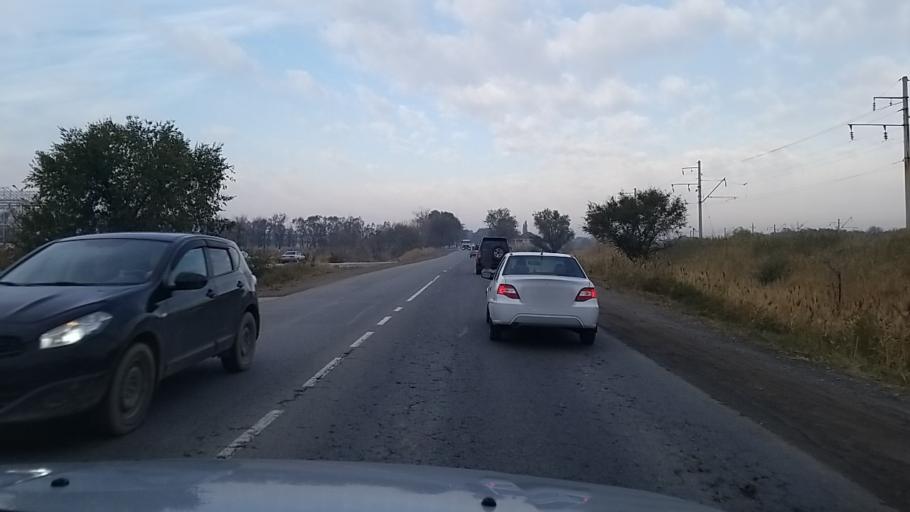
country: KZ
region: Almaty Oblysy
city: Burunday
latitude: 43.3586
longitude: 76.7720
